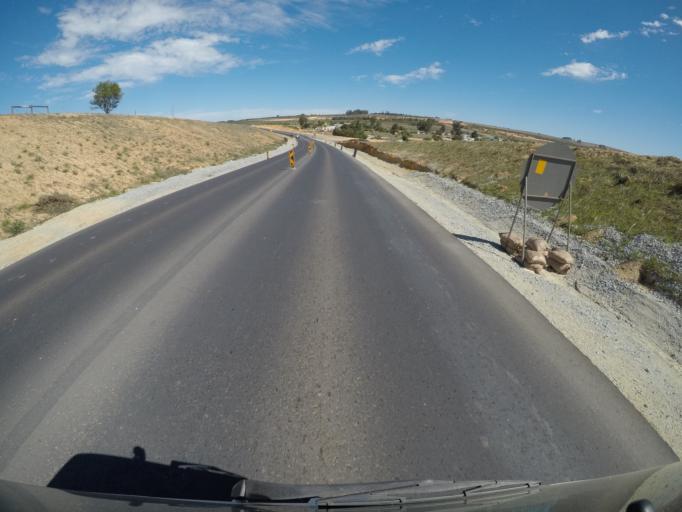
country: ZA
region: Western Cape
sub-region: West Coast District Municipality
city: Malmesbury
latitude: -33.4821
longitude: 18.6783
